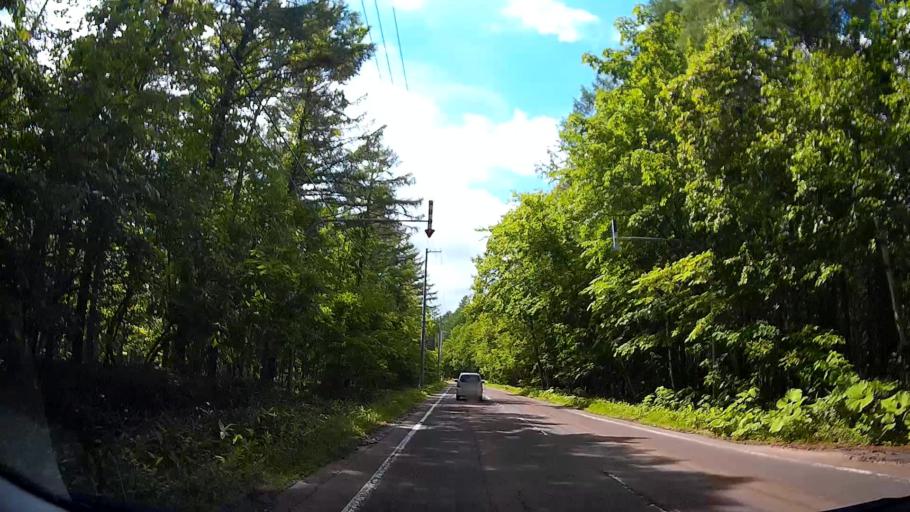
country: JP
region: Hokkaido
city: Kitahiroshima
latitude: 42.8434
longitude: 141.4746
